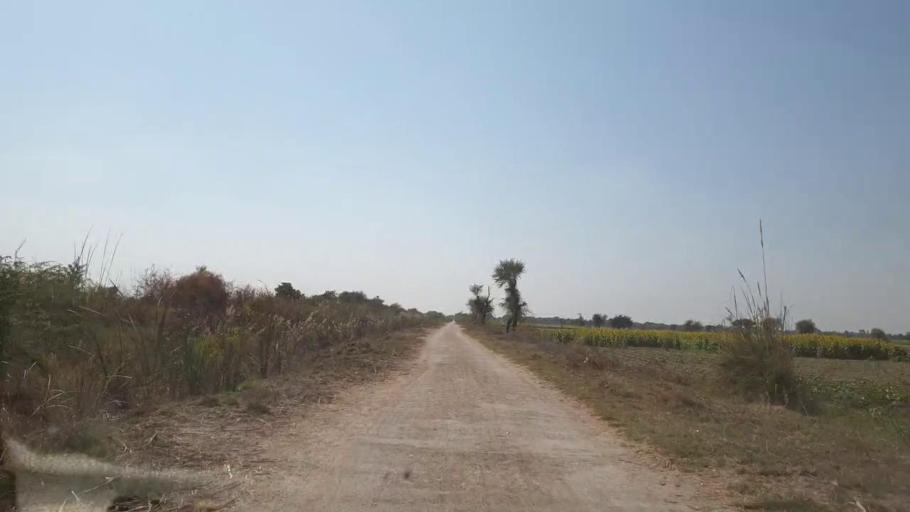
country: PK
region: Sindh
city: Mirpur Khas
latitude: 25.7256
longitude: 69.1094
